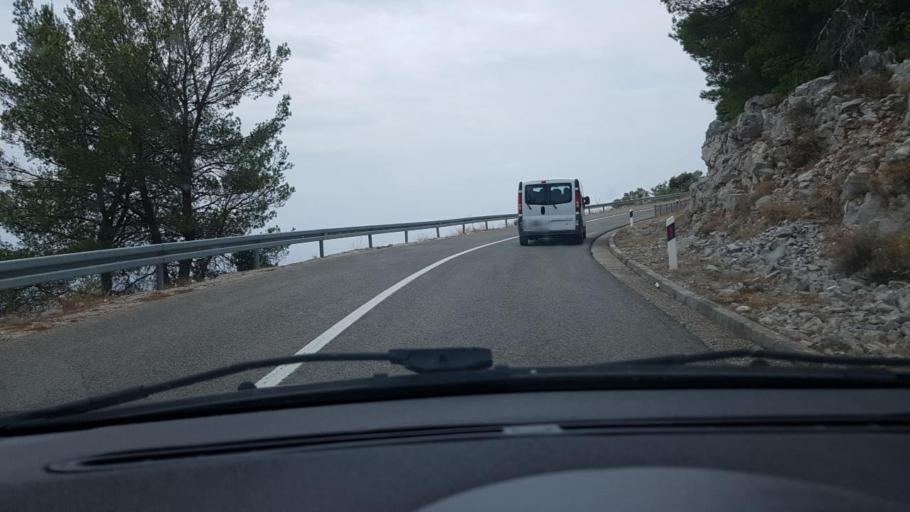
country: HR
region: Dubrovacko-Neretvanska
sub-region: Grad Korcula
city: Zrnovo
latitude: 42.9381
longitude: 17.0228
